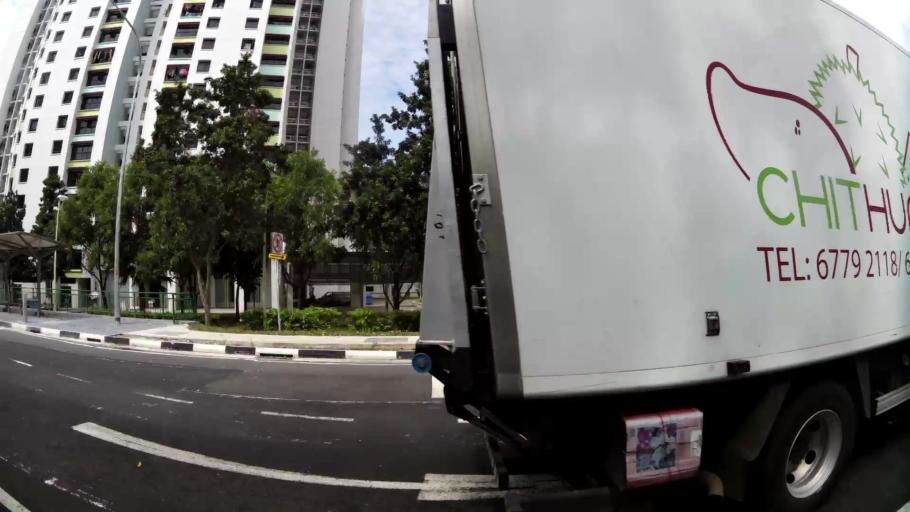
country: SG
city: Singapore
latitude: 1.3116
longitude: 103.7676
